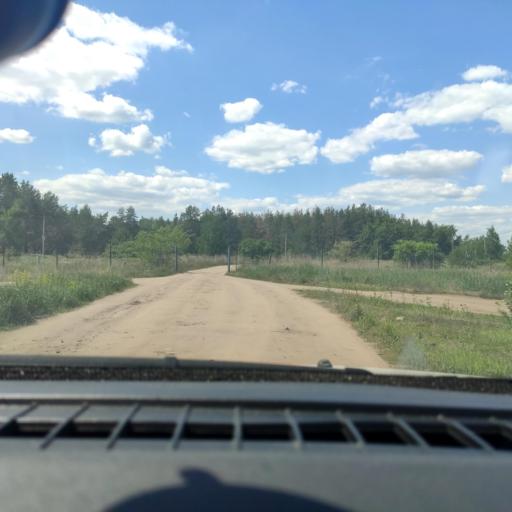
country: RU
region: Voronezj
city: Shilovo
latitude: 51.5346
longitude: 39.1320
